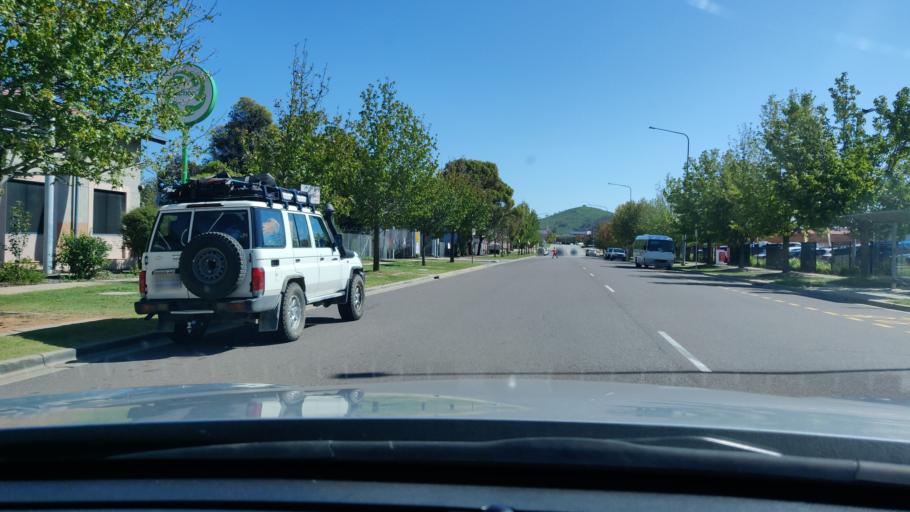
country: AU
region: Australian Capital Territory
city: Macarthur
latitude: -35.4220
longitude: 149.0693
